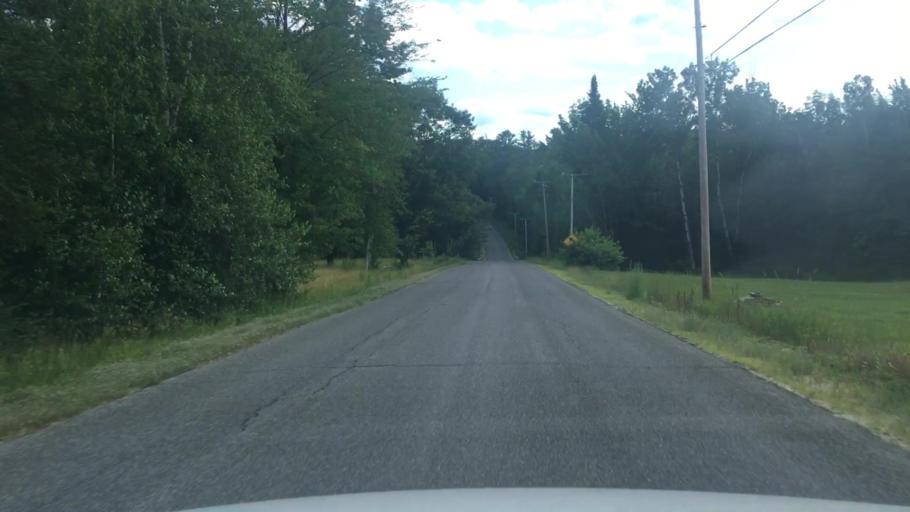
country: US
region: Maine
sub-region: Franklin County
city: Wilton
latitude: 44.6199
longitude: -70.2341
